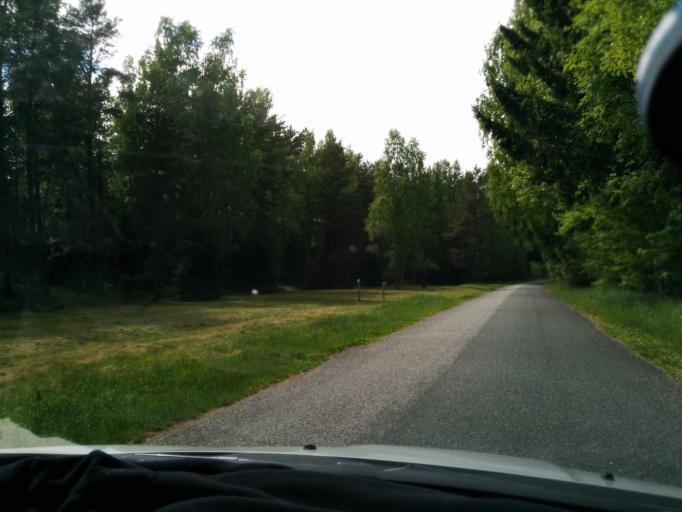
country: EE
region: Harju
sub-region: Loksa linn
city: Loksa
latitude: 59.5623
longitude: 25.6661
